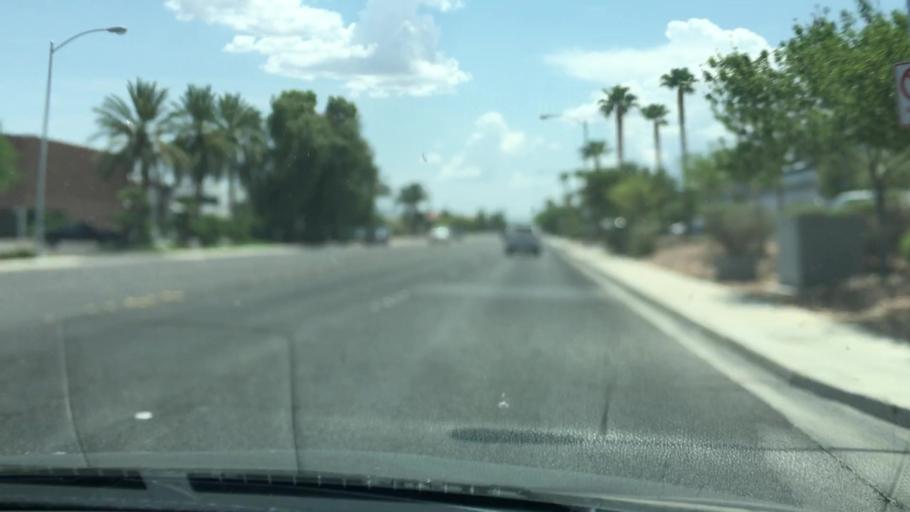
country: US
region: Nevada
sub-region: Clark County
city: Whitney
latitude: 36.0767
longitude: -115.0917
